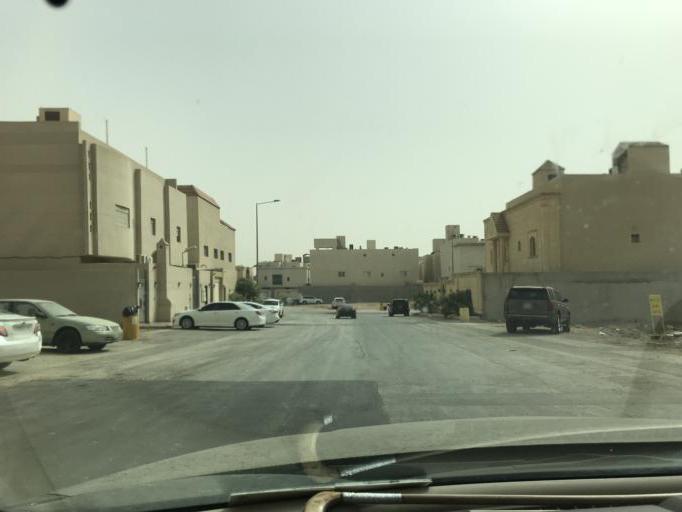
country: SA
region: Ar Riyad
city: Riyadh
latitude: 24.8183
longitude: 46.5986
